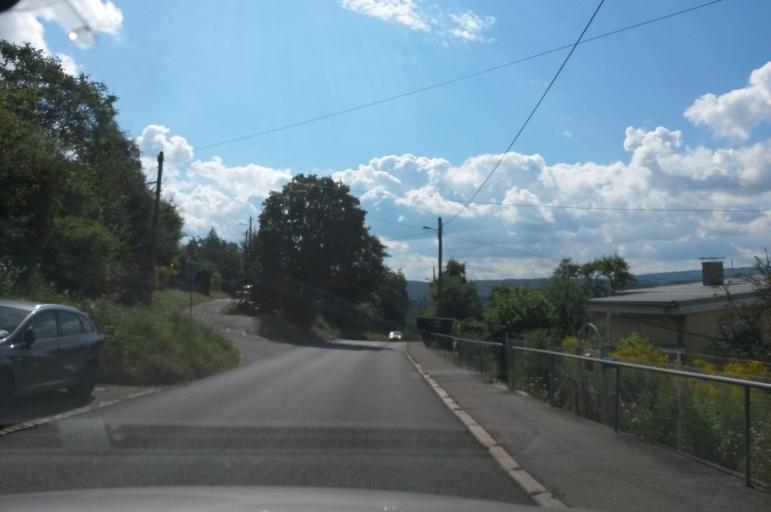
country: DE
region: Baden-Wuerttemberg
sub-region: Karlsruhe Region
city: Ispringen
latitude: 48.8954
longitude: 8.6618
